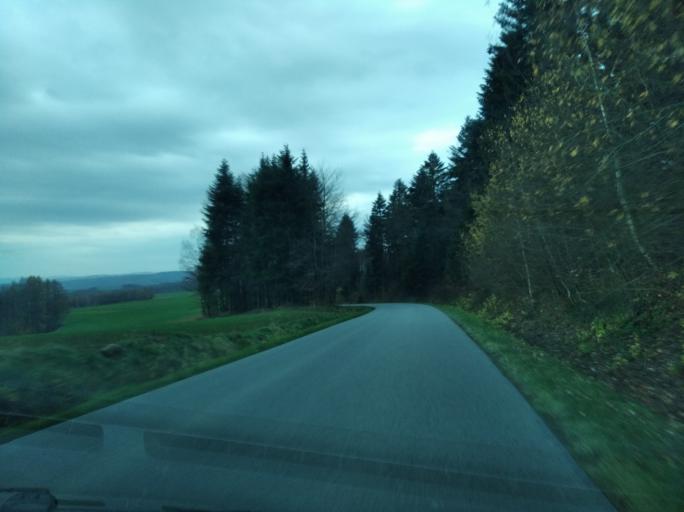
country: PL
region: Subcarpathian Voivodeship
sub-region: Powiat ropczycko-sedziszowski
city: Zagorzyce
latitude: 49.9554
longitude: 21.6944
